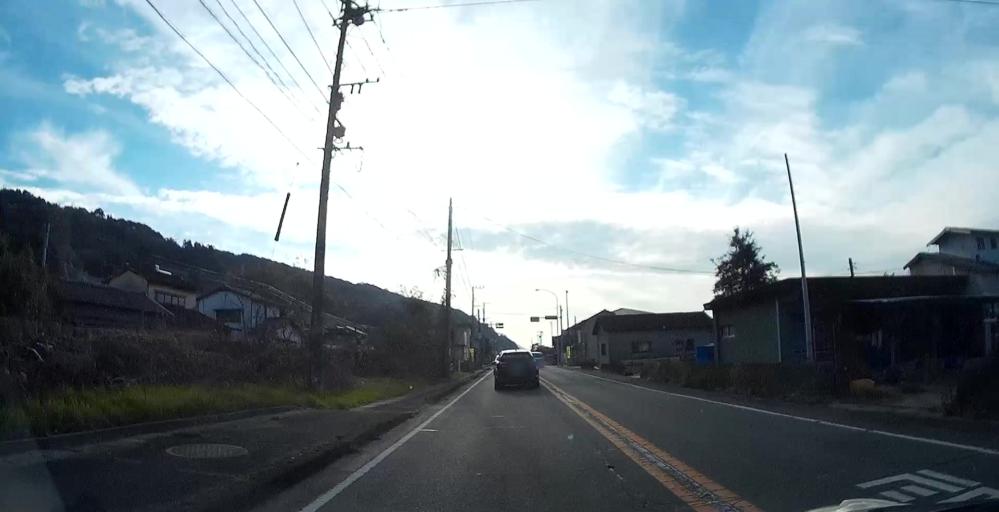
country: JP
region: Kumamoto
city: Uto
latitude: 32.6931
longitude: 130.5635
